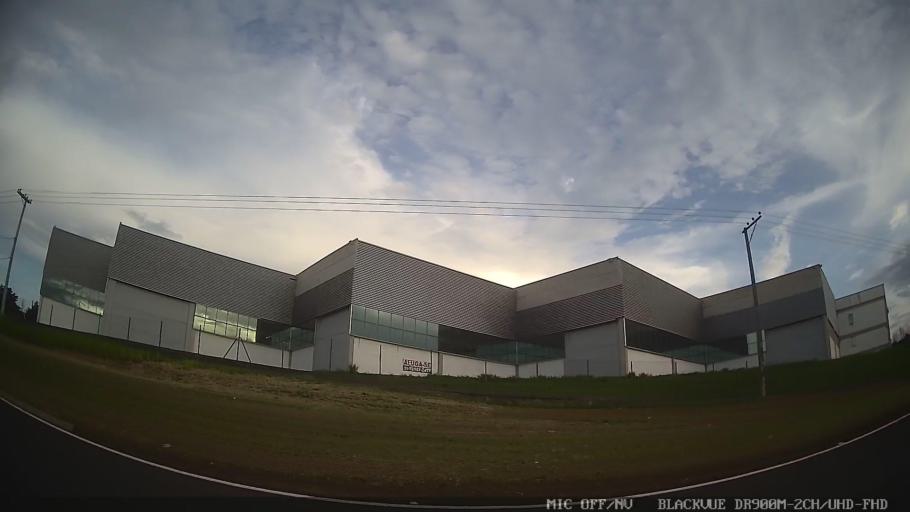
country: BR
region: Sao Paulo
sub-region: Porto Feliz
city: Porto Feliz
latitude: -23.2326
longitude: -47.5128
